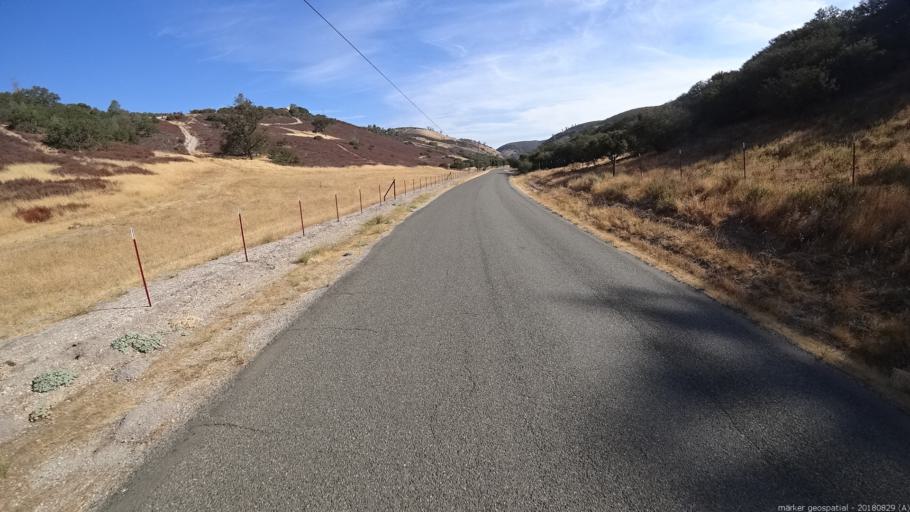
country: US
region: California
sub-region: Monterey County
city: King City
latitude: 35.9834
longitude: -121.0807
